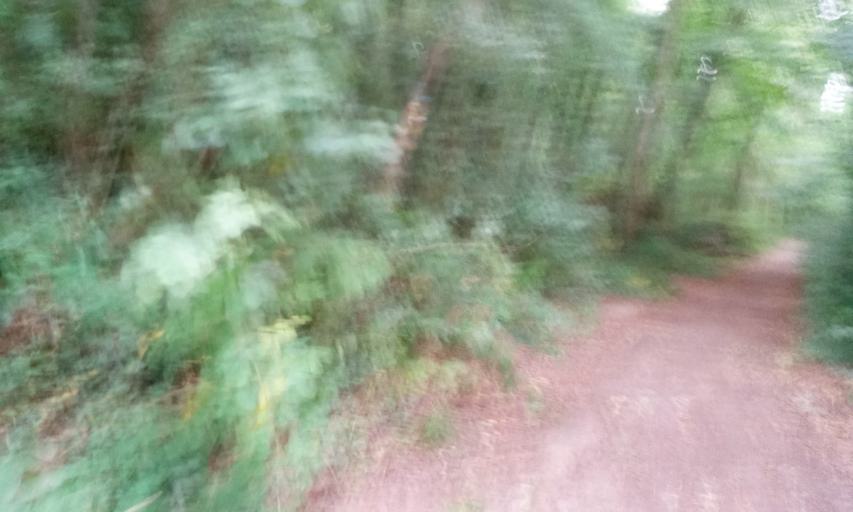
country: FR
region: Lower Normandy
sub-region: Departement du Calvados
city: Mouen
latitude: 49.1456
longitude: -0.4708
